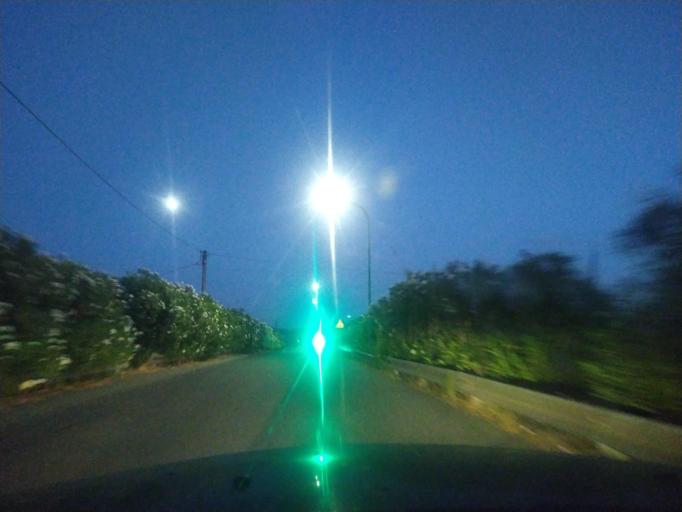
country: IT
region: Sicily
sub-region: Messina
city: Terme
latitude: 38.1430
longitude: 15.1598
